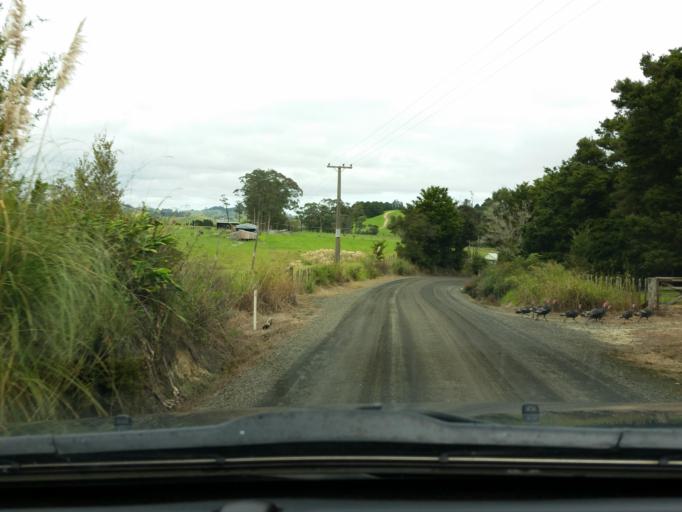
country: NZ
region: Northland
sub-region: Kaipara District
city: Dargaville
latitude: -35.8692
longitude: 174.0141
